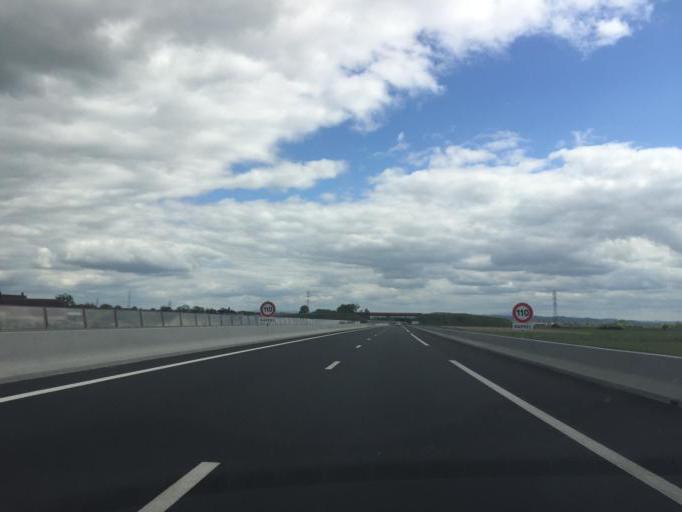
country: FR
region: Auvergne
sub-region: Departement de l'Allier
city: Varennes-sur-Allier
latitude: 46.3099
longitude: 3.3930
